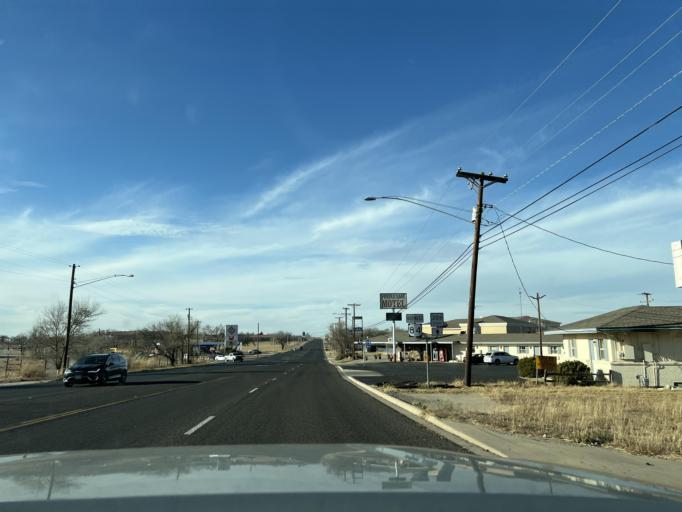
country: US
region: Texas
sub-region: Scurry County
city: Snyder
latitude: 32.7035
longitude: -100.8820
